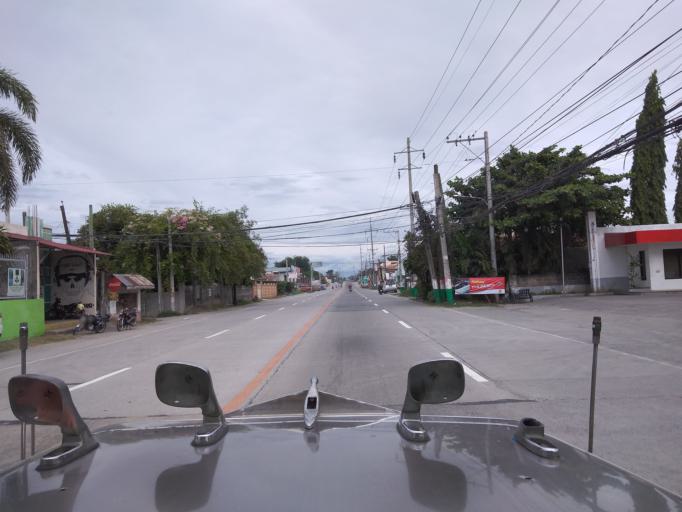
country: PH
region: Central Luzon
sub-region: Province of Pampanga
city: Mexico
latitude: 15.0651
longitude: 120.7235
